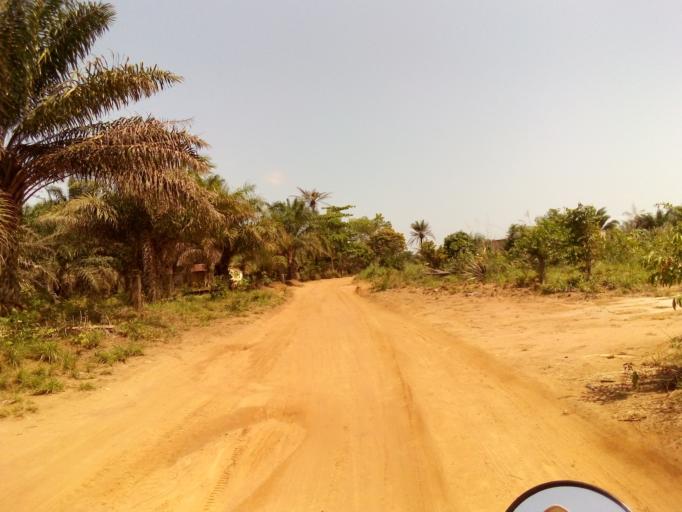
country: SL
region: Western Area
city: Waterloo
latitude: 8.3443
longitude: -13.0131
